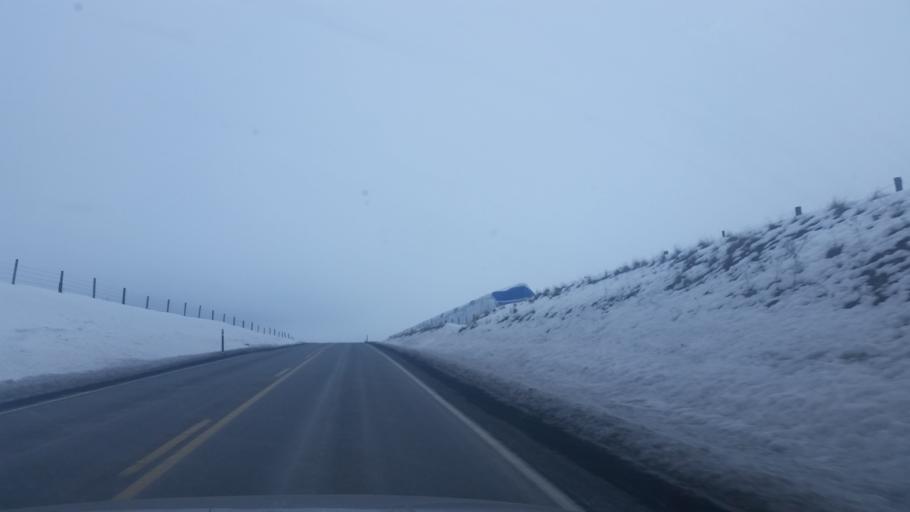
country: US
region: Washington
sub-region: Spokane County
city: Fairchild Air Force Base
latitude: 47.8320
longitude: -117.8751
